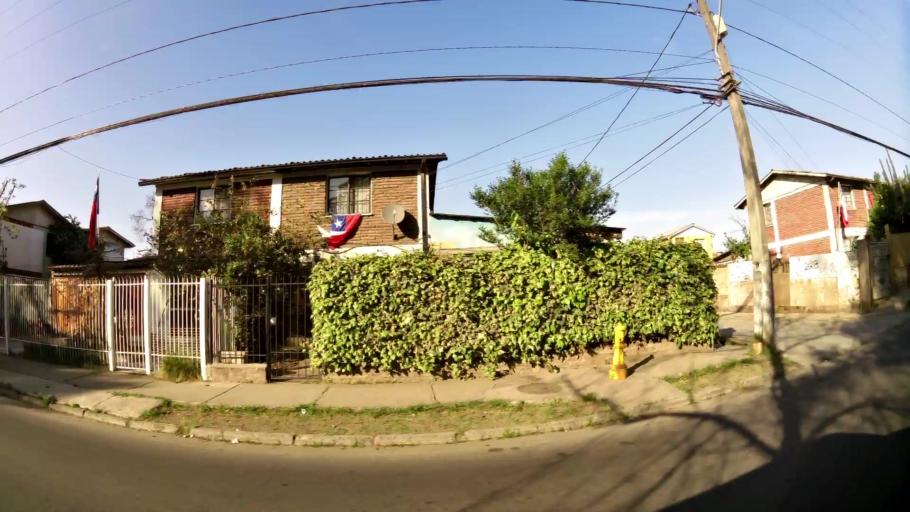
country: CL
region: Santiago Metropolitan
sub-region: Provincia de Santiago
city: Santiago
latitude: -33.3756
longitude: -70.6609
